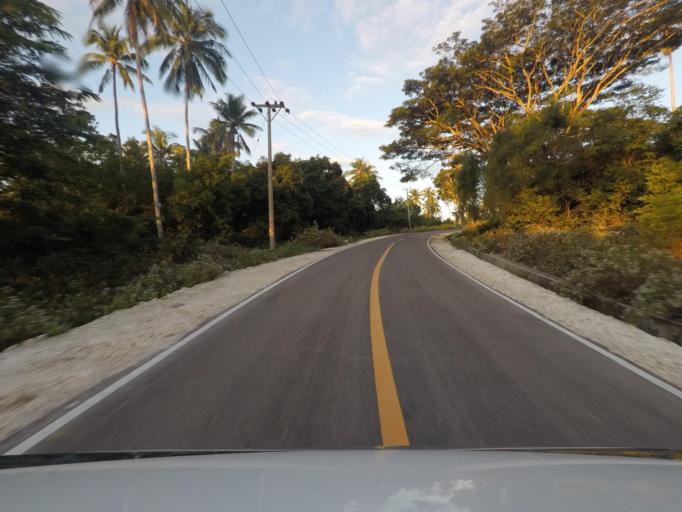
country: TL
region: Lautem
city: Lospalos
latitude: -8.3980
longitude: 127.2737
